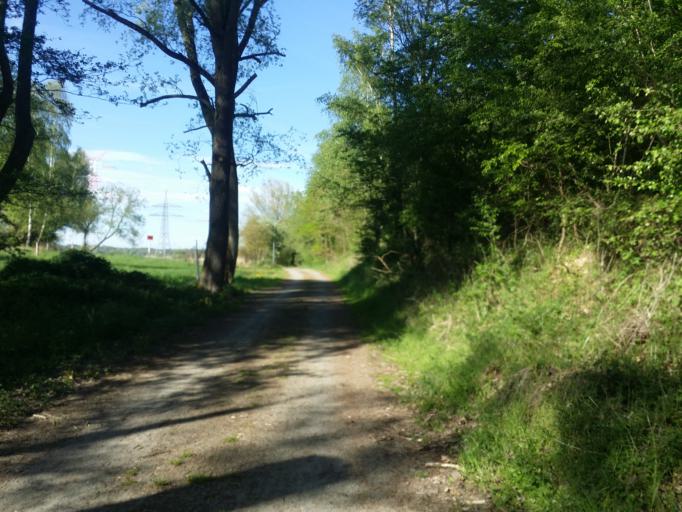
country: DE
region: Lower Saxony
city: Lemwerder
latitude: 53.1317
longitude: 8.6534
